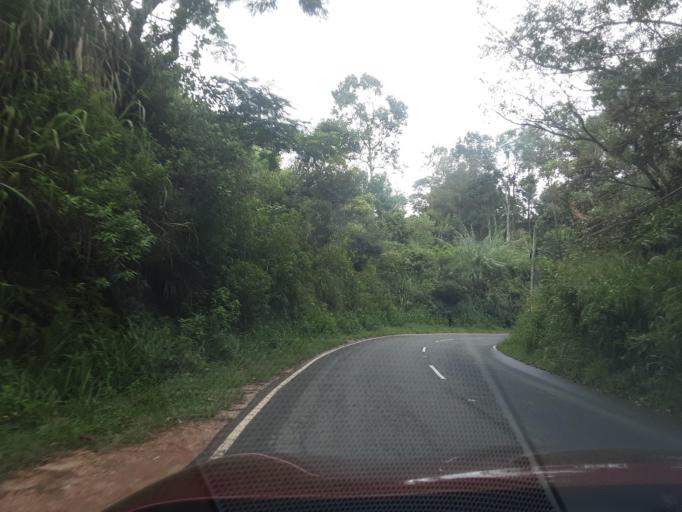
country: LK
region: Uva
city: Haputale
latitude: 6.8546
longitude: 80.9689
